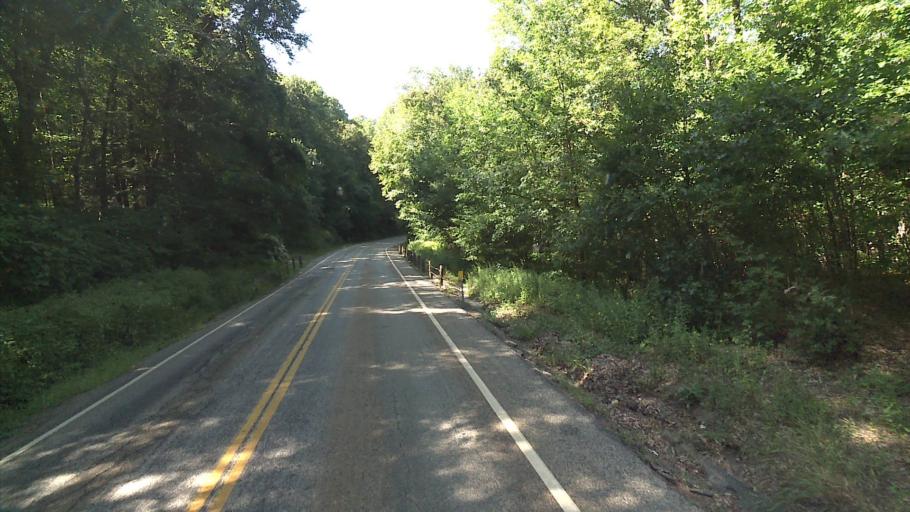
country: US
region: Connecticut
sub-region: Litchfield County
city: Plymouth
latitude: 41.6907
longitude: -73.0606
